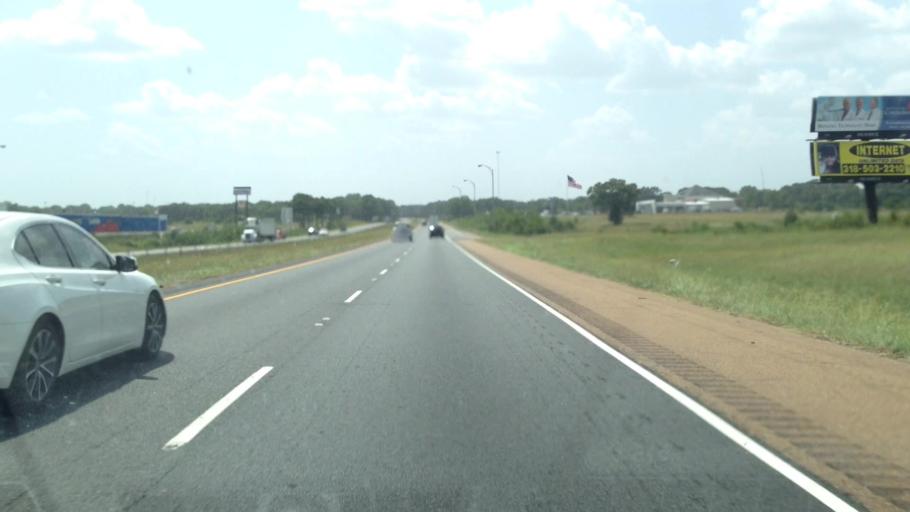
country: US
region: Louisiana
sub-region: Bienville Parish
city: Arcadia
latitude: 32.5638
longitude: -92.9115
